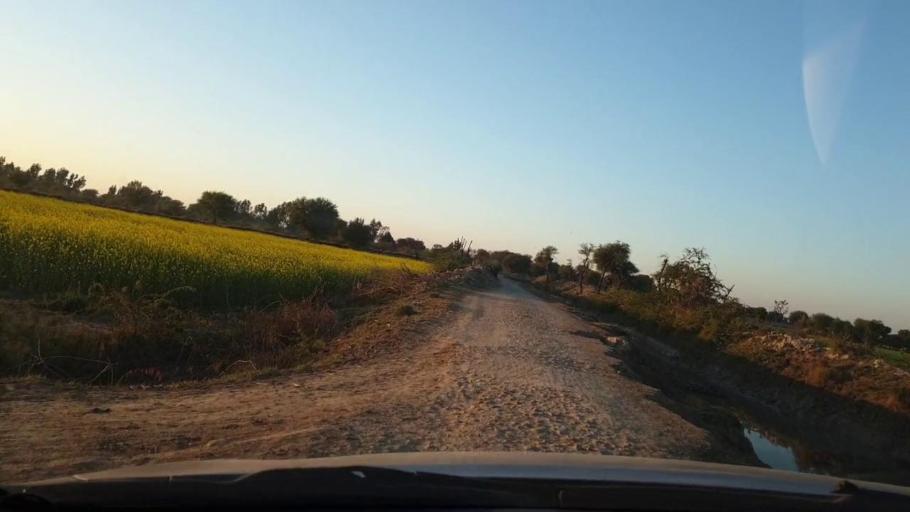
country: PK
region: Sindh
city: Jhol
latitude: 25.8955
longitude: 68.8886
